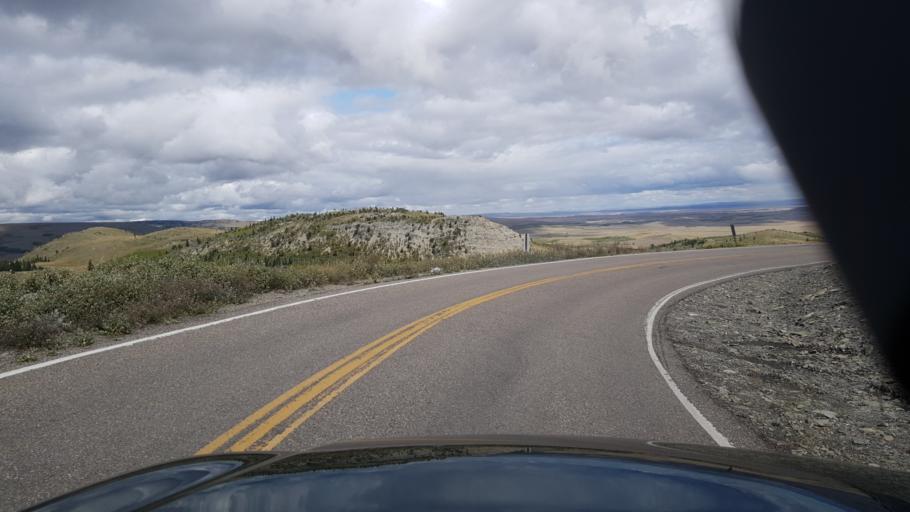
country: US
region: Montana
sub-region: Glacier County
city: South Browning
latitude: 48.5427
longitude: -113.3036
